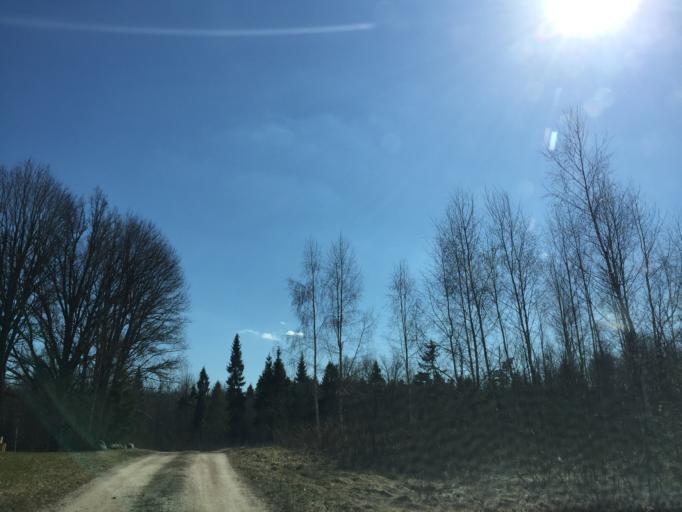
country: EE
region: Viljandimaa
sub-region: Viljandi linn
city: Viljandi
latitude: 58.2743
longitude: 25.6045
